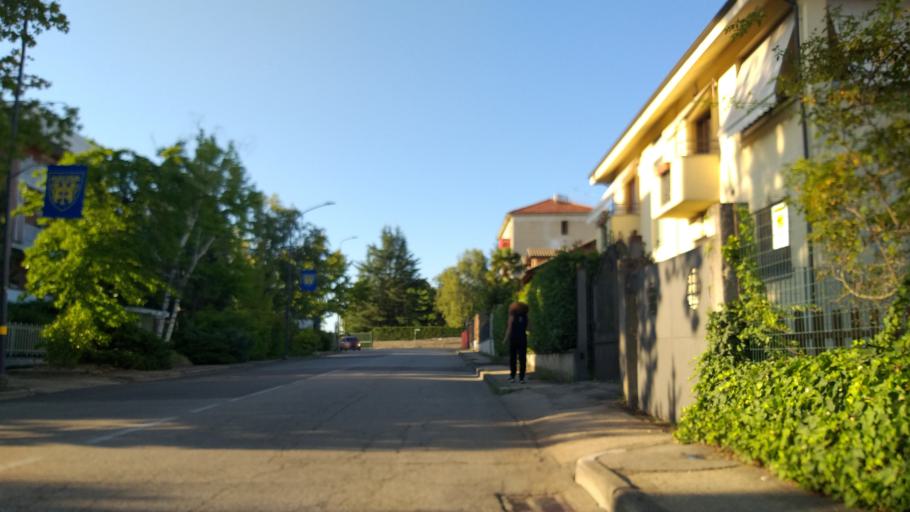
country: IT
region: Piedmont
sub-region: Provincia di Asti
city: Asti
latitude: 44.9092
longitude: 8.2072
